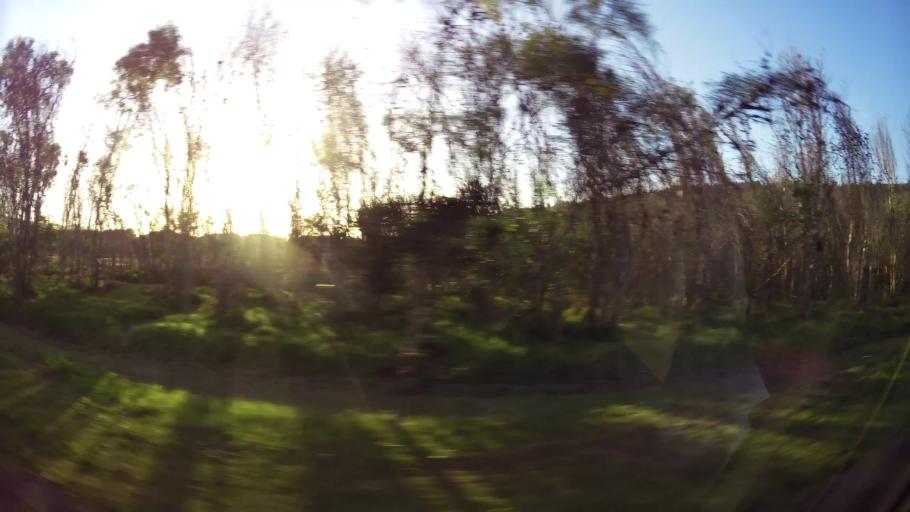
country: ZA
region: Western Cape
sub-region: Eden District Municipality
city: Knysna
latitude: -34.0128
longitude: 22.7900
